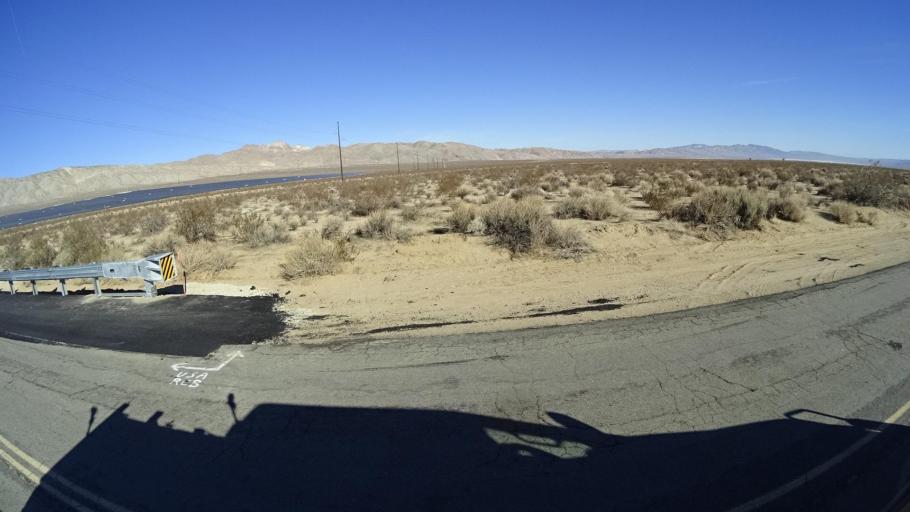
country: US
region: California
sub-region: Kern County
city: California City
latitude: 35.1980
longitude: -118.0562
